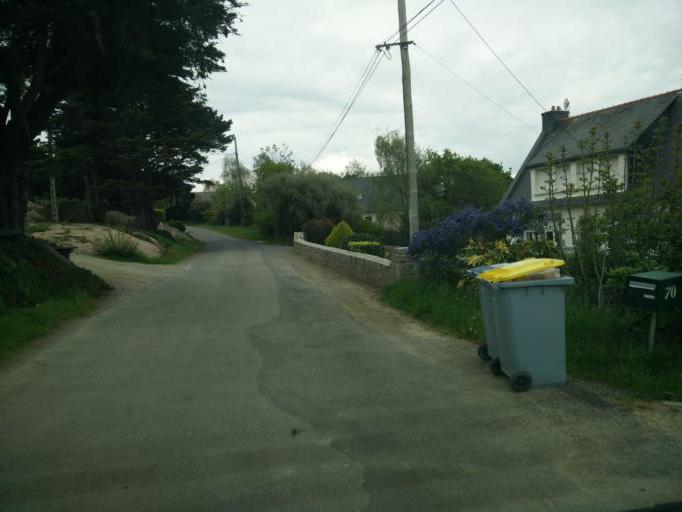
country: FR
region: Brittany
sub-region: Departement des Cotes-d'Armor
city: Tregastel
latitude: 48.8213
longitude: -3.4895
